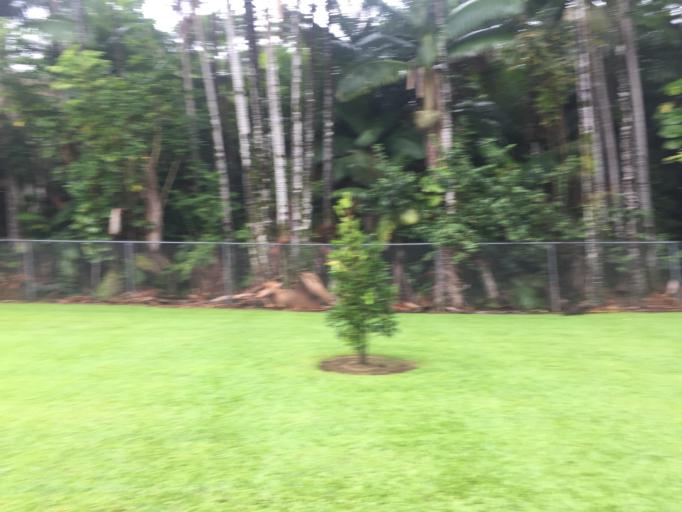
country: US
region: Hawaii
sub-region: Hawaii County
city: Hilo
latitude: 19.7147
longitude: -155.1313
